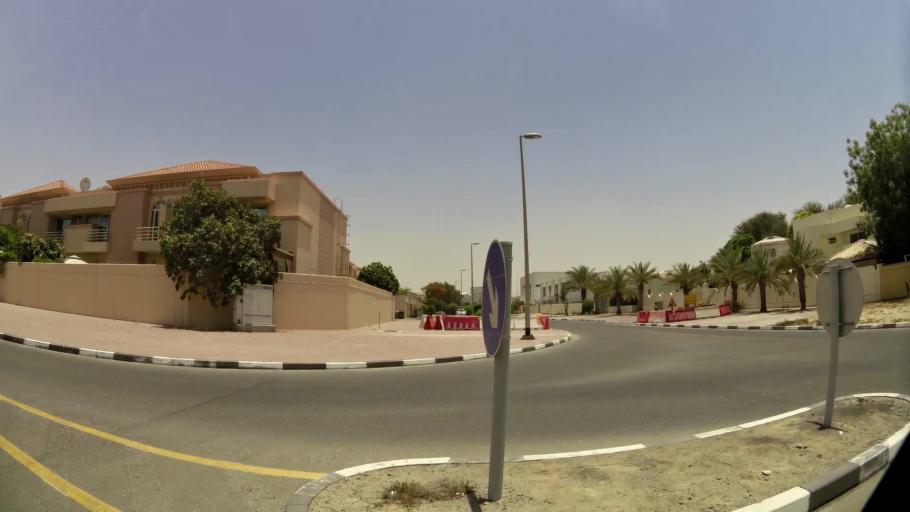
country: AE
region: Dubai
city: Dubai
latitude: 25.1712
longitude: 55.2374
